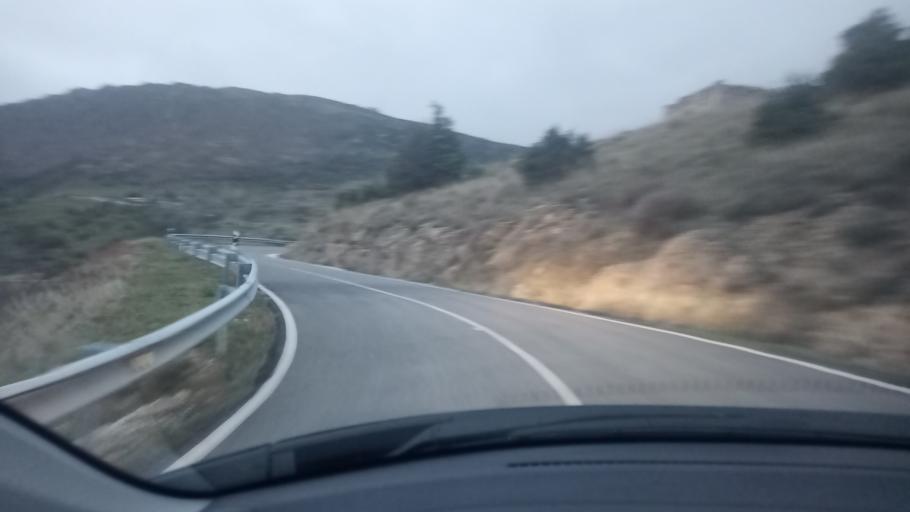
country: ES
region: Madrid
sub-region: Provincia de Madrid
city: Zarzalejo
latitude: 40.5557
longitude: -4.1949
